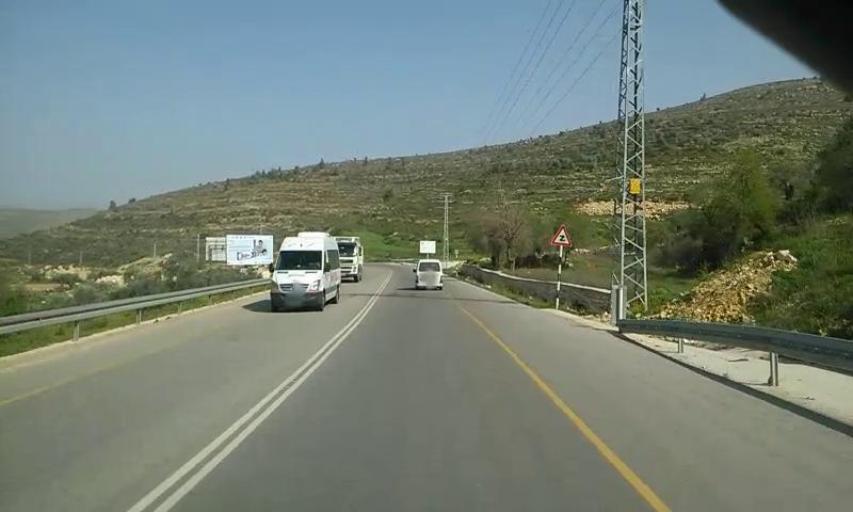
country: PS
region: West Bank
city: Dura al Qar`
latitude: 31.9808
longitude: 35.2352
